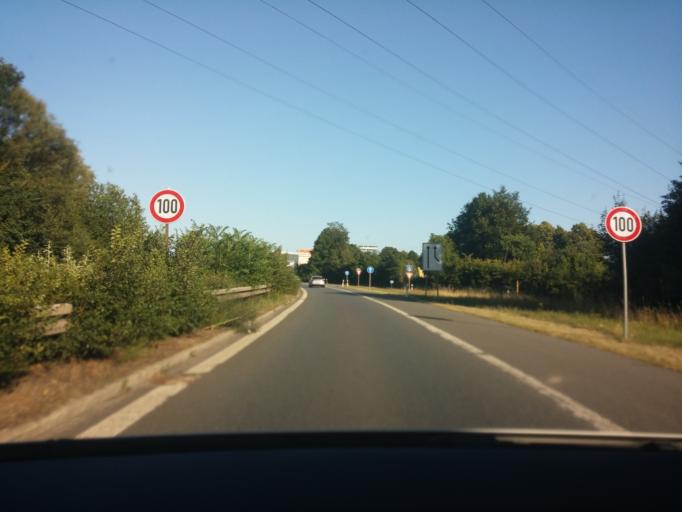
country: DE
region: Bavaria
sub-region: Regierungsbezirk Unterfranken
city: Kleinostheim
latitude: 49.9908
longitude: 9.0748
